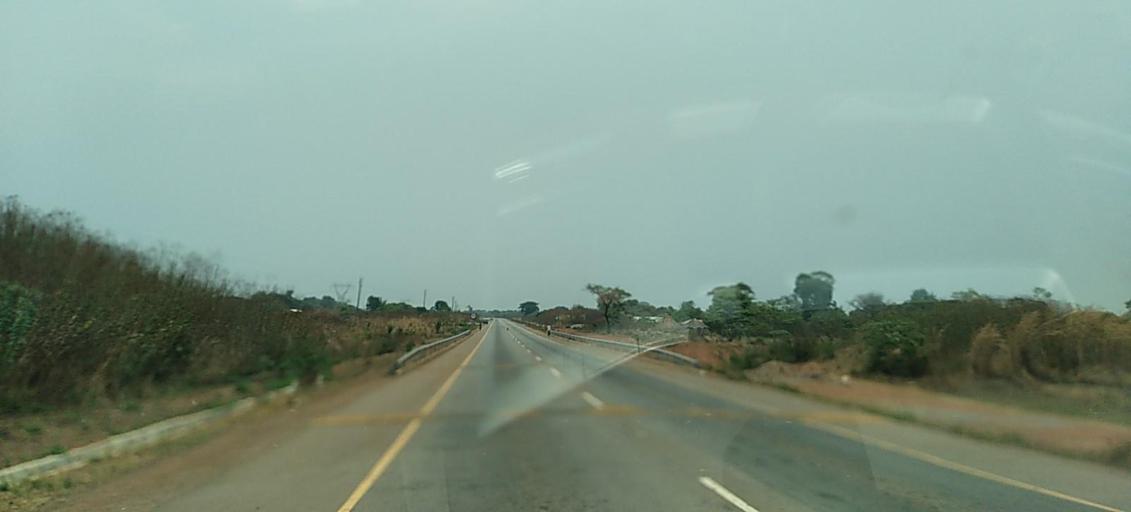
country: ZM
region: Copperbelt
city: Chililabombwe
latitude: -12.3823
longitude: 27.3240
